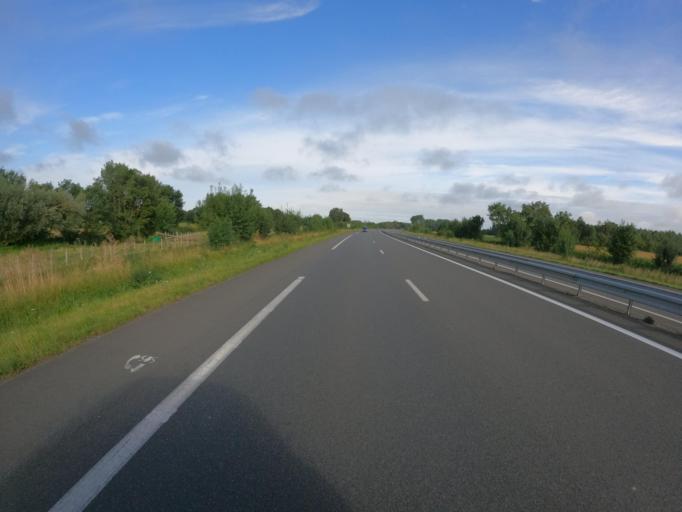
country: FR
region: Pays de la Loire
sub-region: Departement de Maine-et-Loire
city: Villebernier
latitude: 47.2951
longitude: -0.0234
